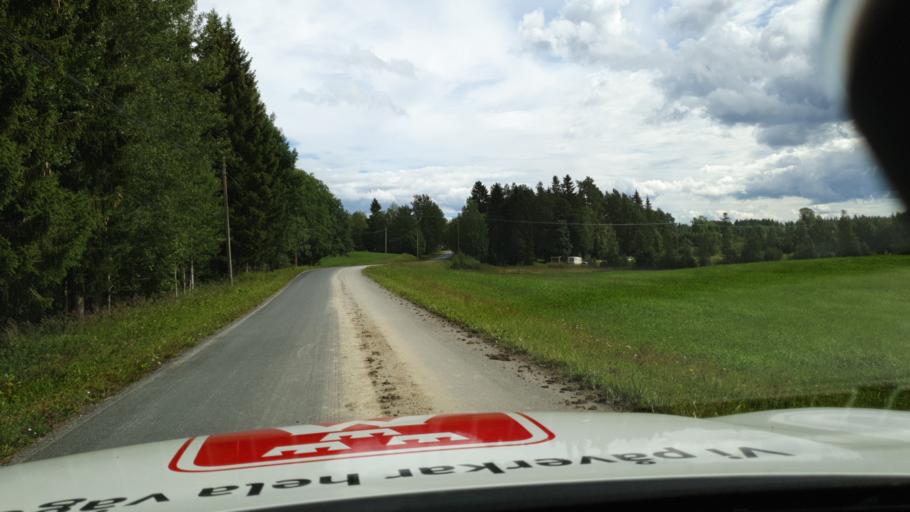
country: SE
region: Jaemtland
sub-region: Krokoms Kommun
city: Valla
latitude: 63.2686
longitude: 13.9481
